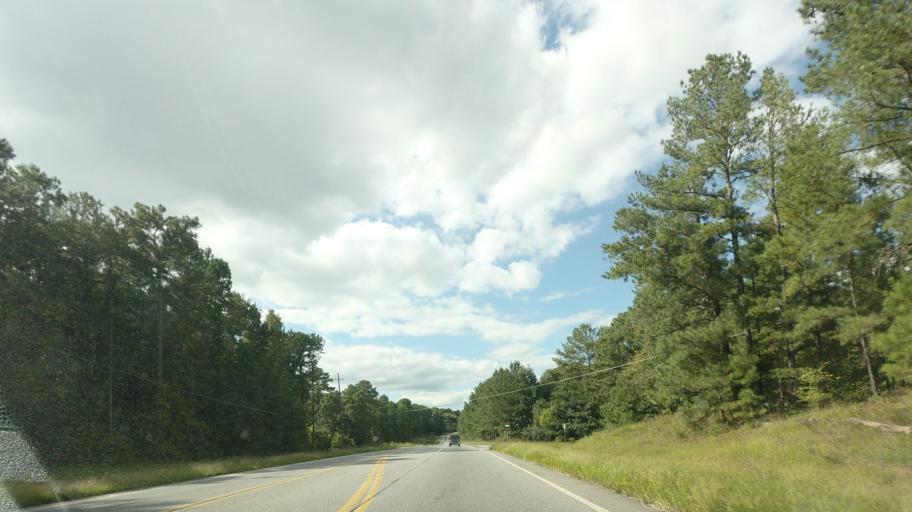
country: US
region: Georgia
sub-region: Bibb County
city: Macon
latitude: 32.9437
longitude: -83.7223
